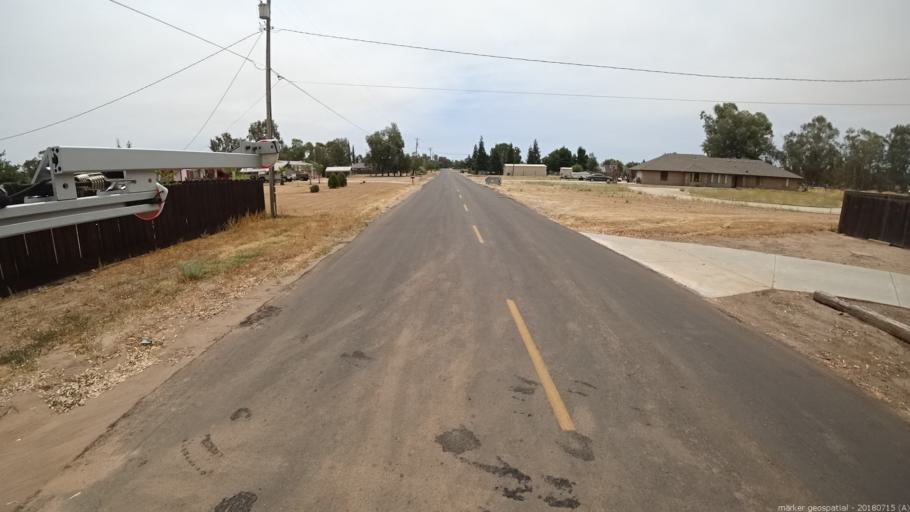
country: US
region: California
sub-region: Madera County
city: Madera Acres
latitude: 37.0125
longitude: -120.0893
